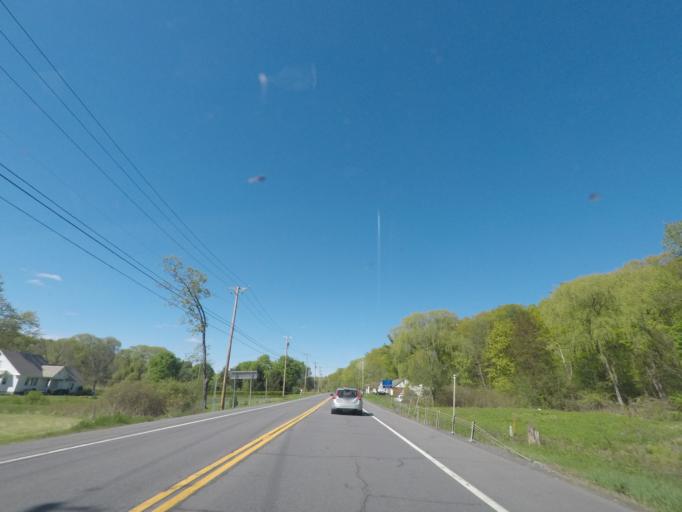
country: US
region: New York
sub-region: Albany County
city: Ravena
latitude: 42.4264
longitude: -73.8171
